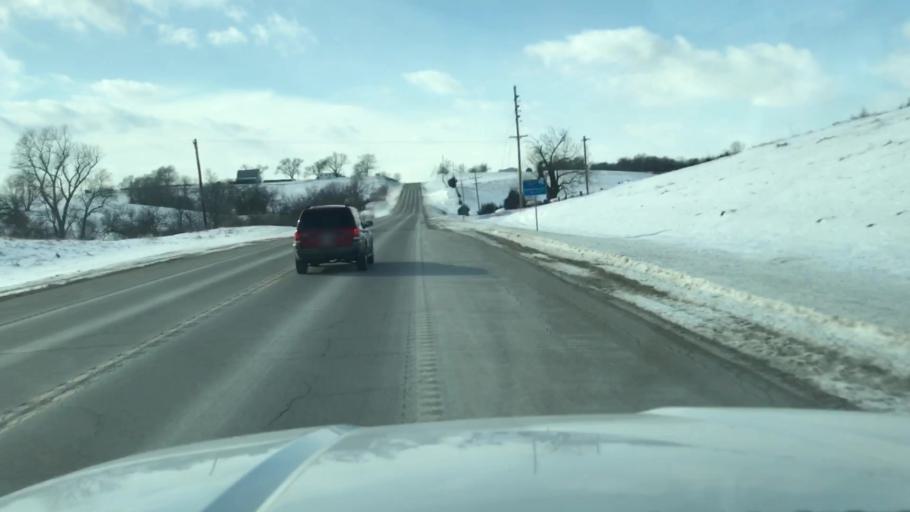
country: US
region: Missouri
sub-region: Nodaway County
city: Maryville
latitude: 40.3436
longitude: -94.6971
